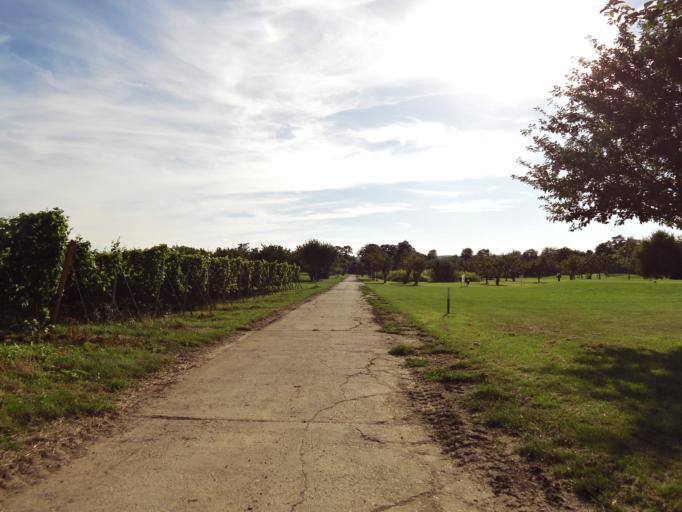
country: DE
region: Rheinland-Pfalz
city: Bissersheim
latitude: 49.5276
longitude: 8.1979
